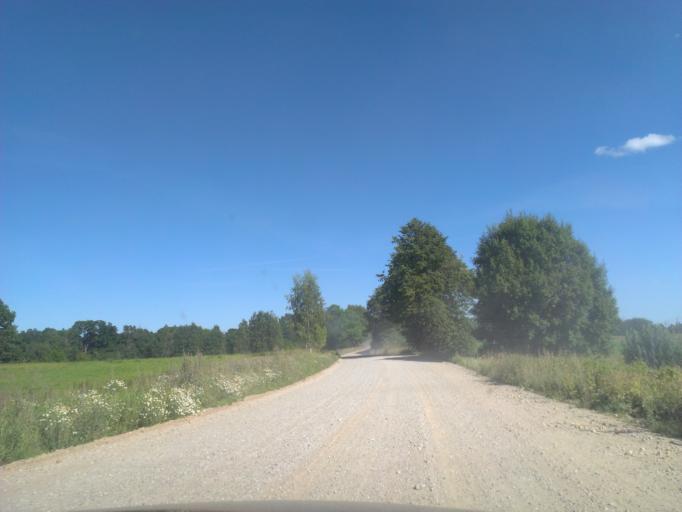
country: LV
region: Malpils
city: Malpils
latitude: 57.0597
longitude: 25.1516
